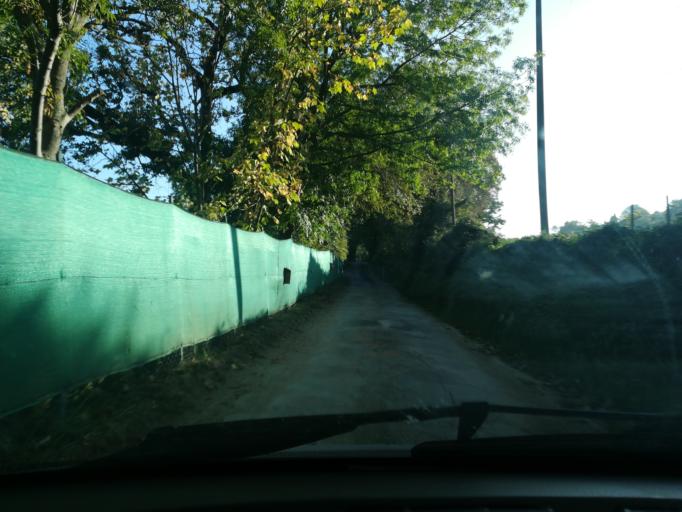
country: IT
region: The Marches
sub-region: Provincia di Macerata
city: Macerata
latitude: 43.2815
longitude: 13.4530
